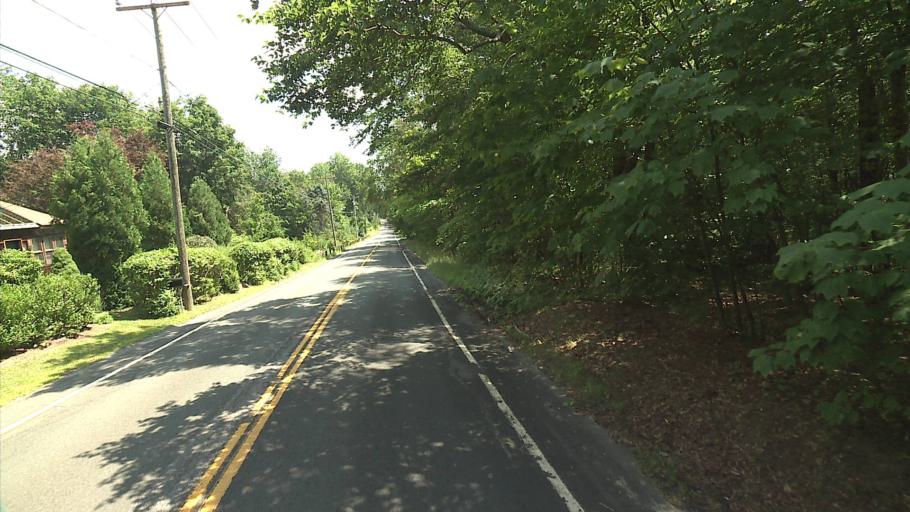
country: US
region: Connecticut
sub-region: Litchfield County
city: Winchester Center
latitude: 41.9874
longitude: -73.1302
